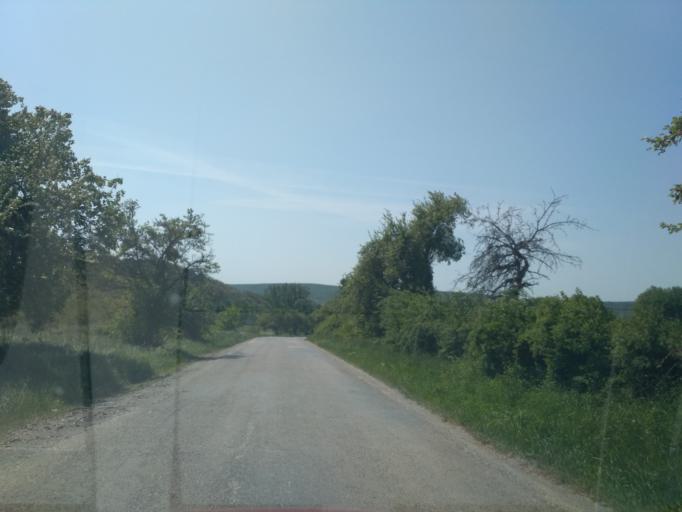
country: SK
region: Kosicky
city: Kosice
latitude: 48.7882
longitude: 21.3438
